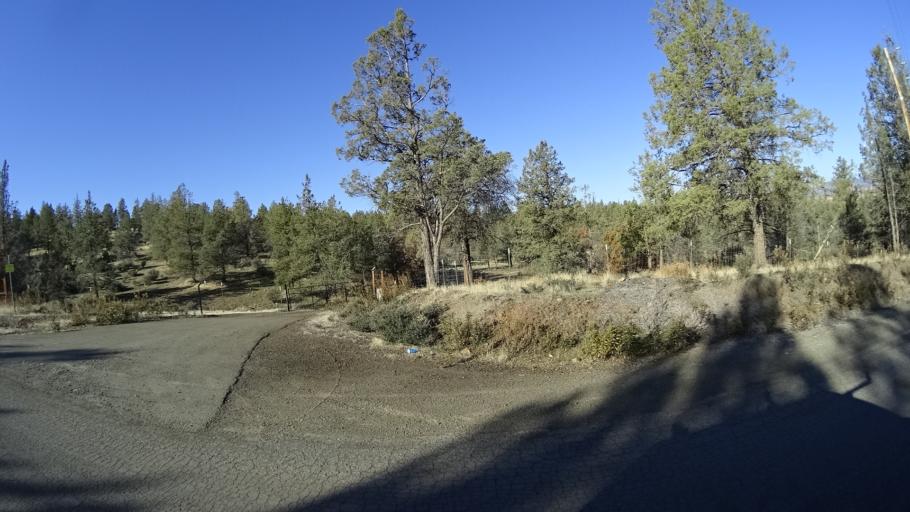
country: US
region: California
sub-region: Siskiyou County
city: Montague
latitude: 41.8844
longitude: -122.4458
